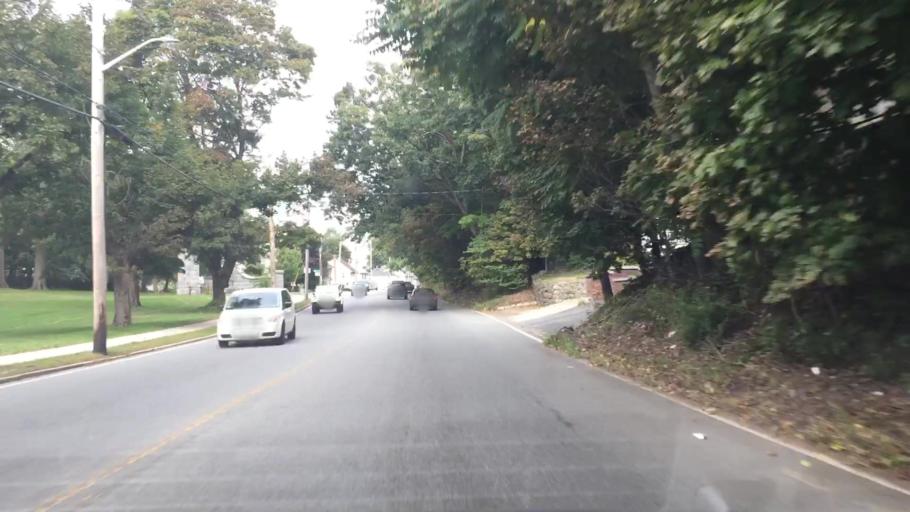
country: US
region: Massachusetts
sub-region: Middlesex County
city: Lowell
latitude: 42.6330
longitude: -71.2892
